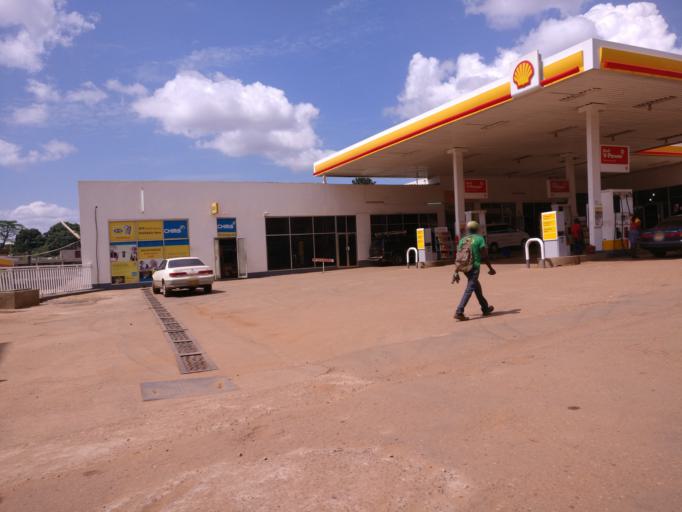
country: UG
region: Central Region
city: Kampala Central Division
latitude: 0.3074
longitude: 32.5624
